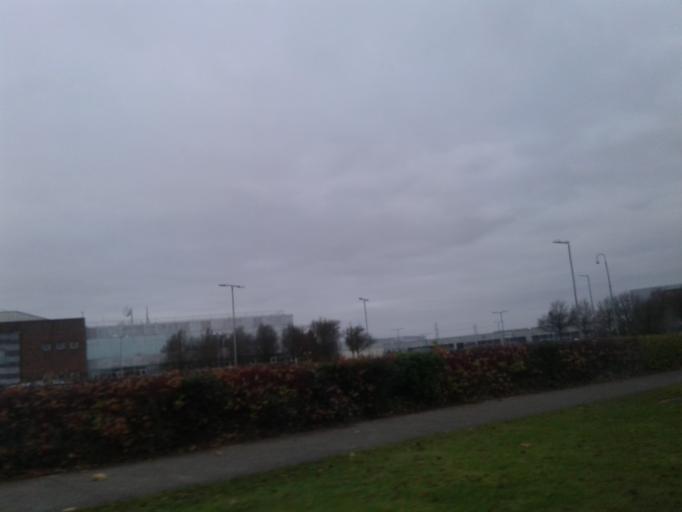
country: IE
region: Leinster
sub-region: Fingal County
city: Blanchardstown
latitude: 53.4070
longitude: -6.3550
